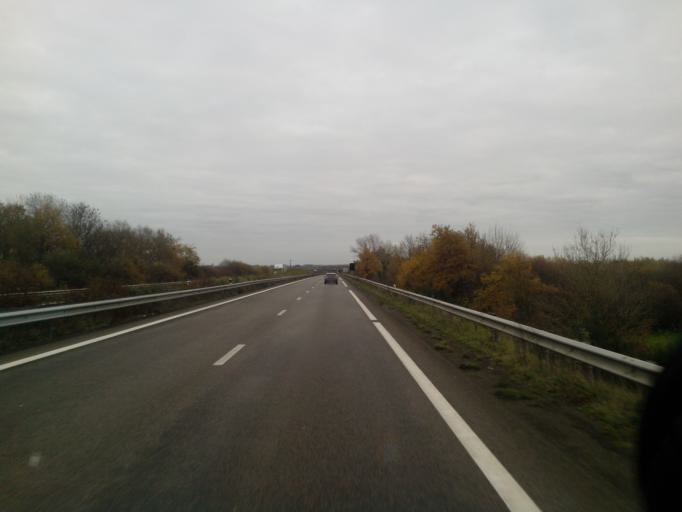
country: FR
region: Pays de la Loire
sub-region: Departement de la Loire-Atlantique
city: Le Pallet
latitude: 47.1563
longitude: -1.3289
